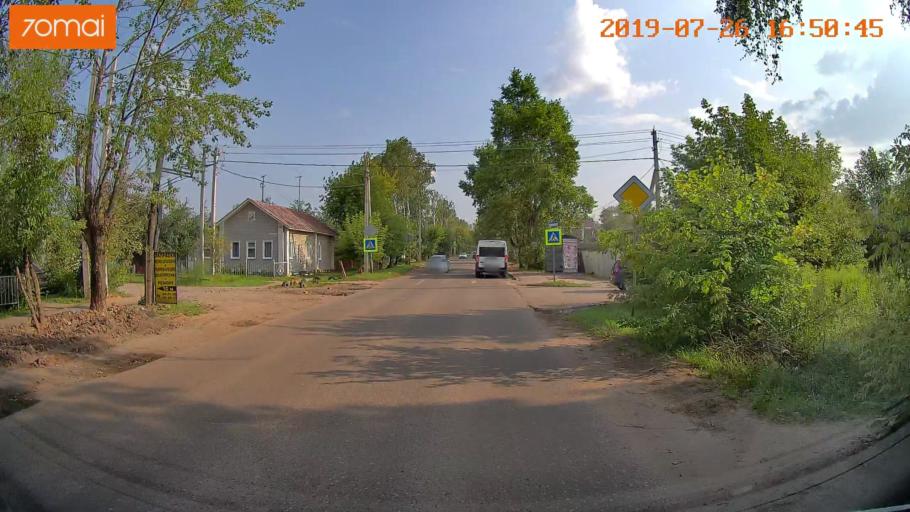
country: RU
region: Ivanovo
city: Bogorodskoye
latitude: 57.0221
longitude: 41.0207
